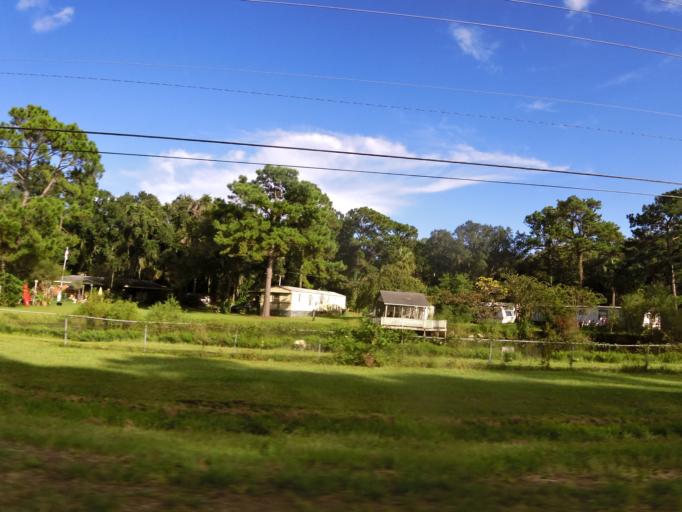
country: US
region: Georgia
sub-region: Glynn County
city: Country Club Estates
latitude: 31.2502
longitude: -81.4457
